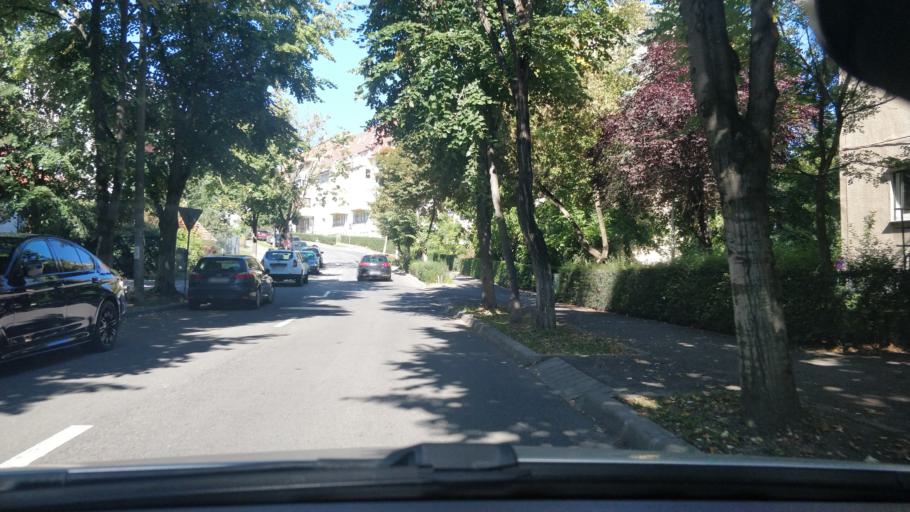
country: RO
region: Cluj
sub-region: Municipiul Cluj-Napoca
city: Cluj-Napoca
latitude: 46.7572
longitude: 23.5822
